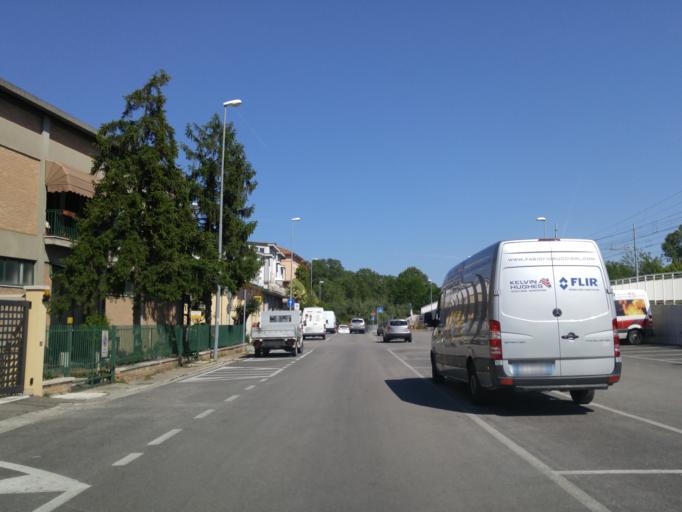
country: IT
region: The Marches
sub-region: Provincia di Pesaro e Urbino
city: Pesaro
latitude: 43.9084
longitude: 12.8951
